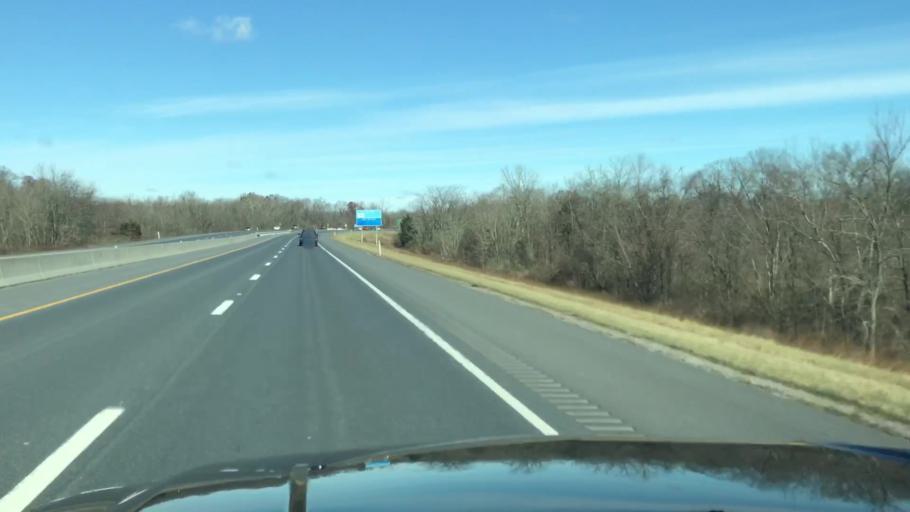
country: US
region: Pennsylvania
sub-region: Snyder County
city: Selinsgrove
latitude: 40.7692
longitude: -76.8664
